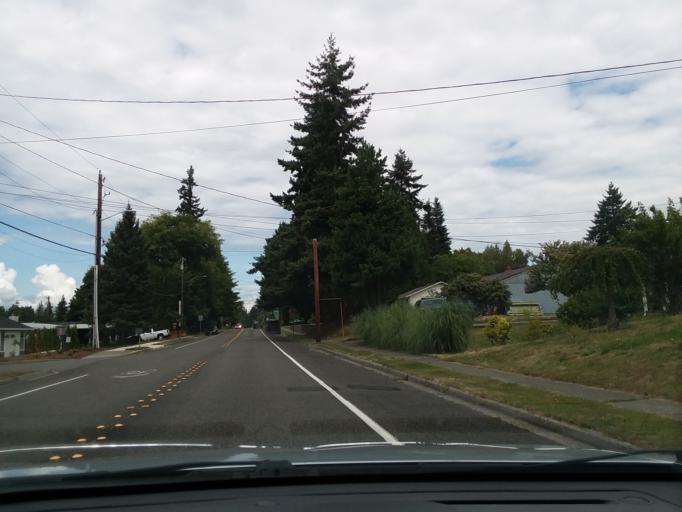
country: US
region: Washington
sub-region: Snohomish County
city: Alderwood Manor
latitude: 47.8270
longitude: -122.2978
